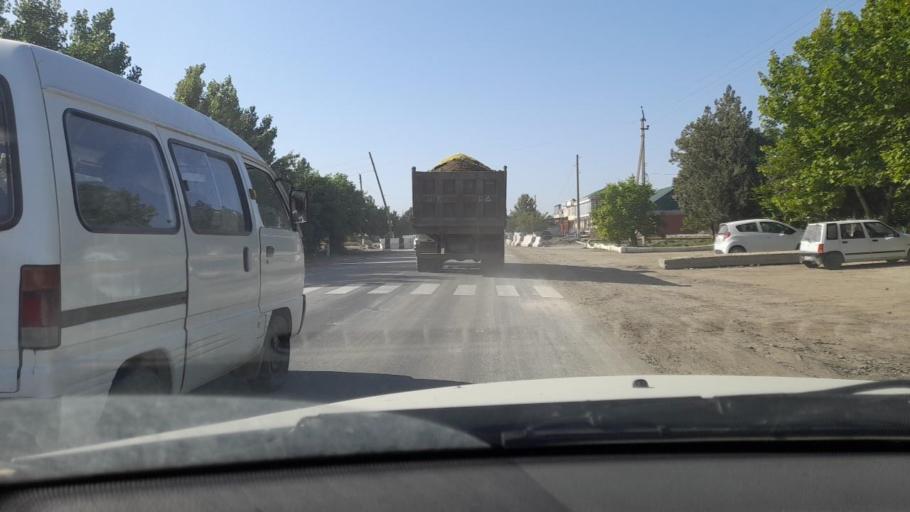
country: UZ
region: Bukhara
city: Romiton
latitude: 40.0484
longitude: 64.3286
